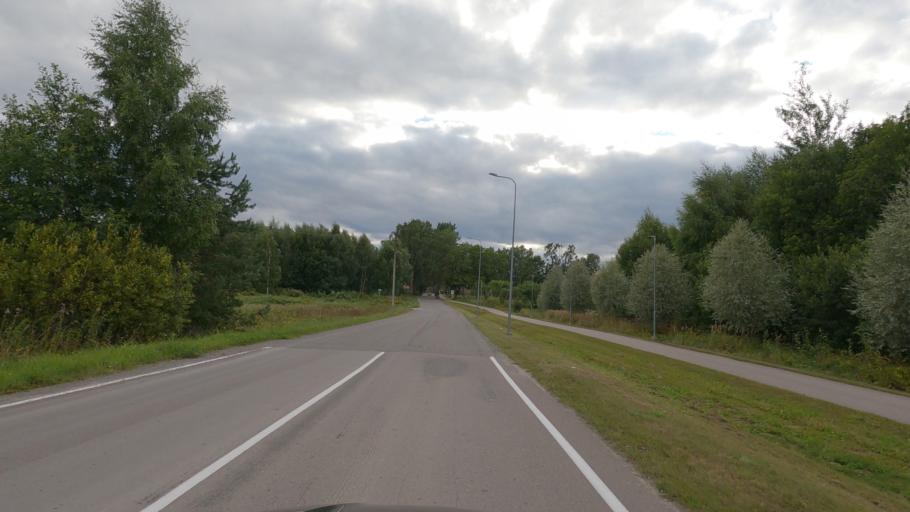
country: EE
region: Raplamaa
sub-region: Kohila vald
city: Kohila
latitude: 59.1763
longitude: 24.7612
